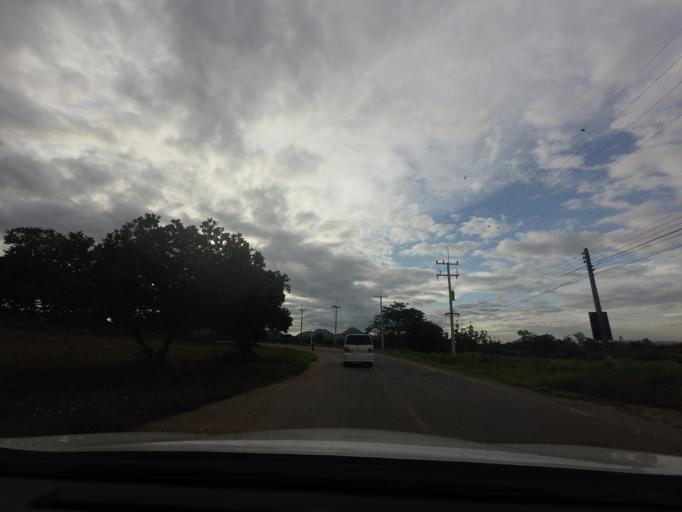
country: TH
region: Nakhon Ratchasima
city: Pak Chong
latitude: 14.6082
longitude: 101.4235
